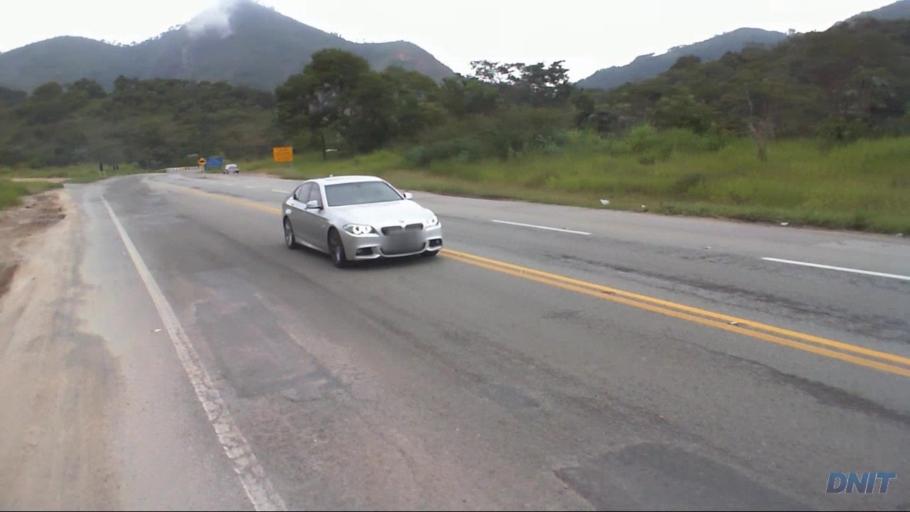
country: BR
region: Minas Gerais
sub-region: Nova Era
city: Nova Era
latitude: -19.6583
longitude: -42.9609
